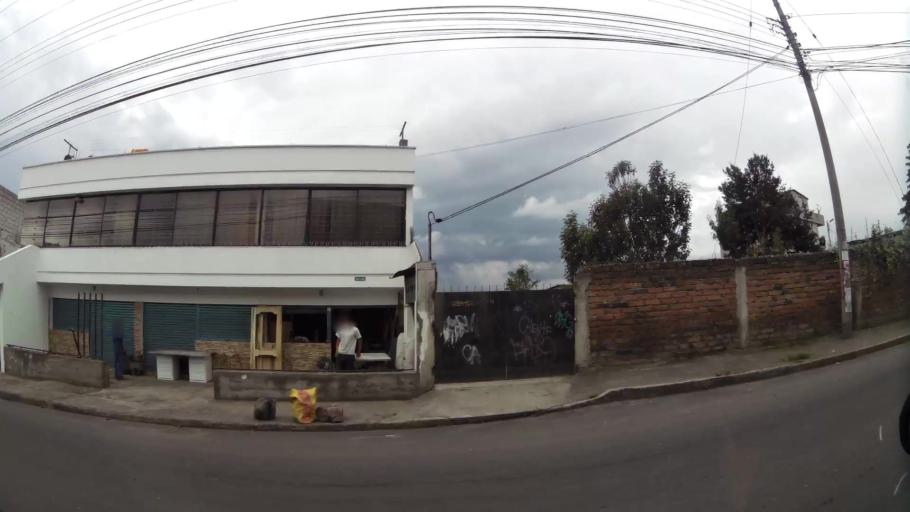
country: EC
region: Pichincha
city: Sangolqui
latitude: -0.3385
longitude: -78.5538
